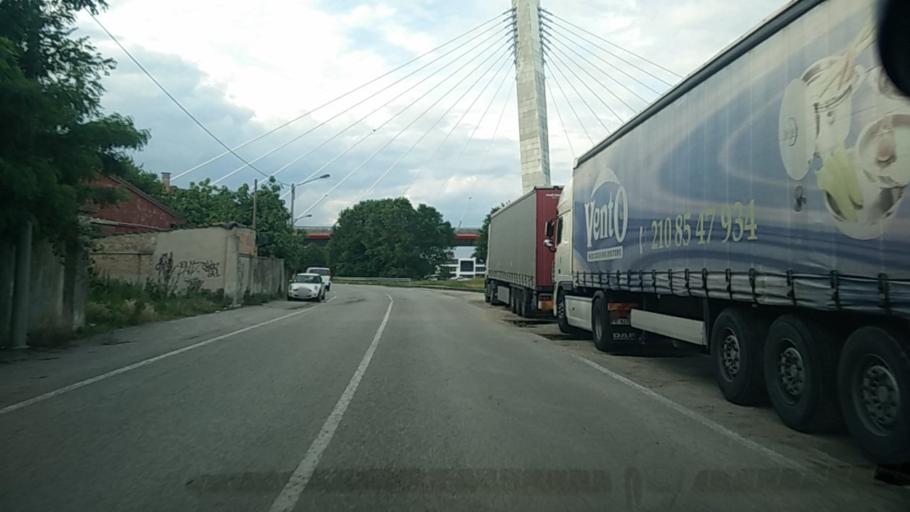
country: IT
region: Veneto
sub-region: Provincia di Venezia
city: Mestre
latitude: 45.4715
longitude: 12.2360
